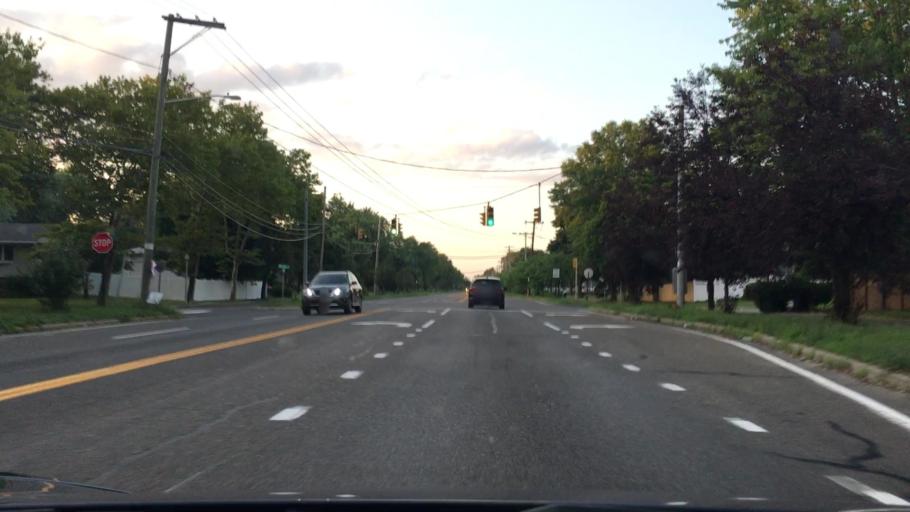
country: US
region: New York
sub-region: Suffolk County
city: Dix Hills
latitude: 40.7952
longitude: -73.2976
